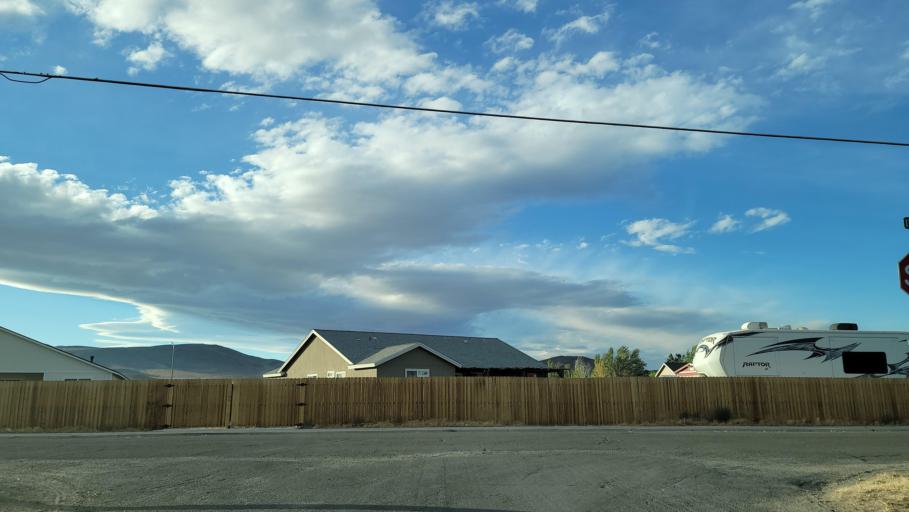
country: US
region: Nevada
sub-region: Lyon County
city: Silver Springs
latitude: 39.4005
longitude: -119.2374
